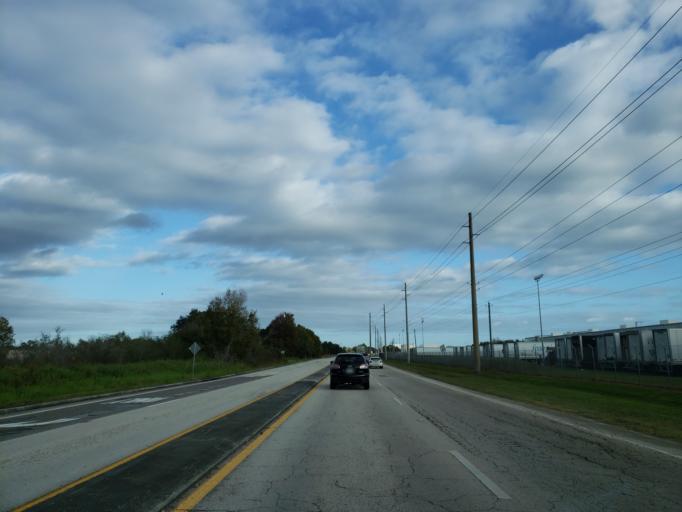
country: US
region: Florida
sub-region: Hillsborough County
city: Plant City
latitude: 27.9903
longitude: -82.1047
